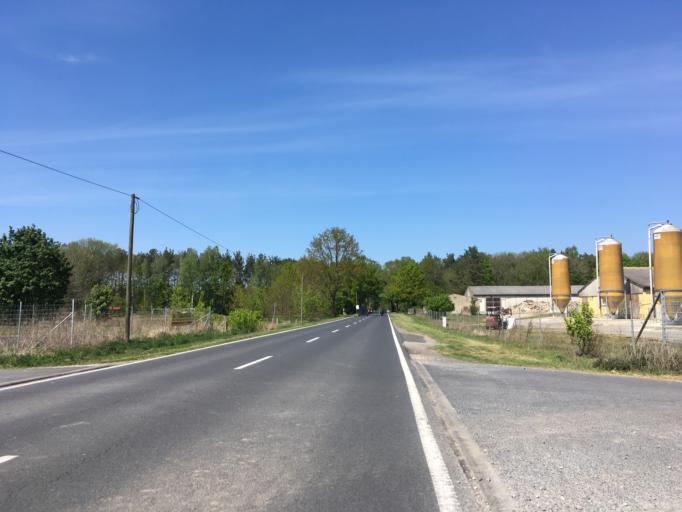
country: DE
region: Brandenburg
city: Rudnitz
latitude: 52.7647
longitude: 13.5655
